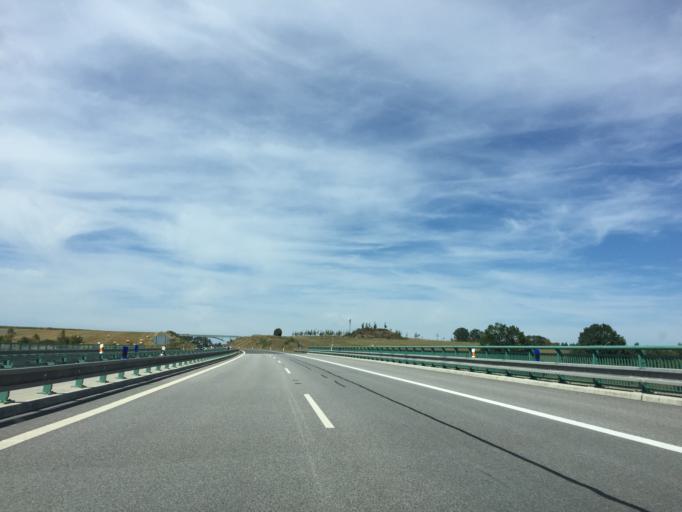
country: CZ
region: Jihocesky
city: Sobeslav
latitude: 49.2799
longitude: 14.7371
